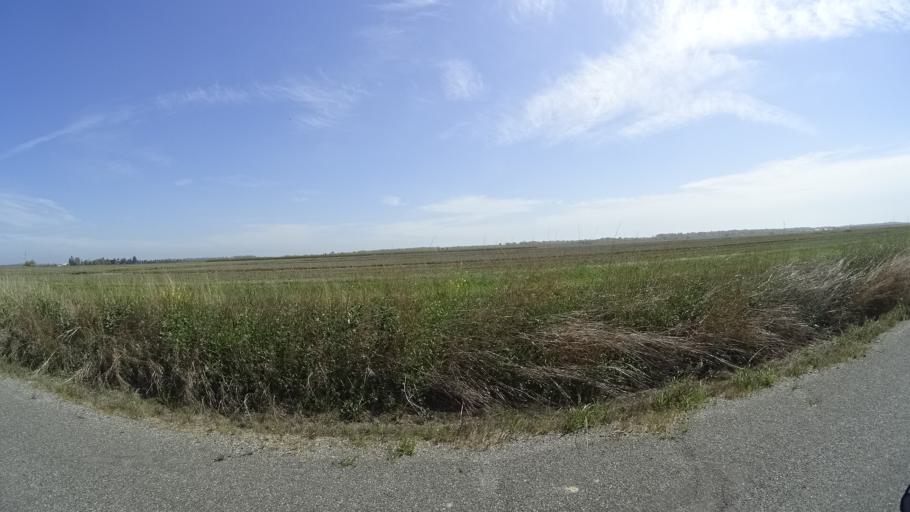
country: US
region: California
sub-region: Glenn County
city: Hamilton City
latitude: 39.5970
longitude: -122.0276
